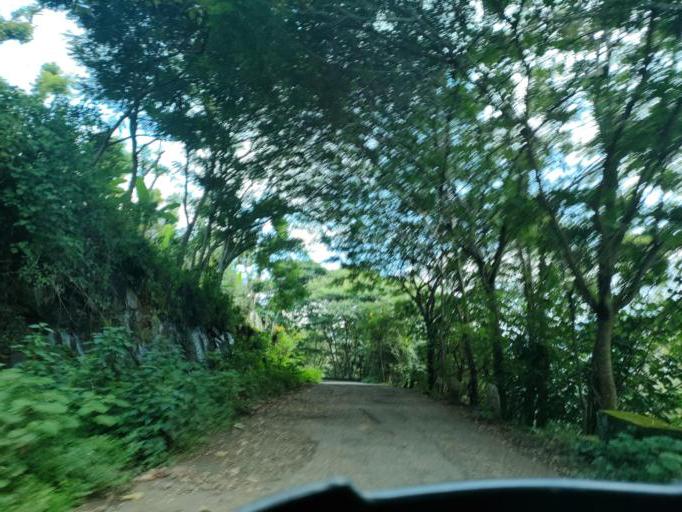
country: IN
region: Tamil Nadu
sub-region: Dindigul
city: Kodaikanal
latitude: 10.2882
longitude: 77.5289
